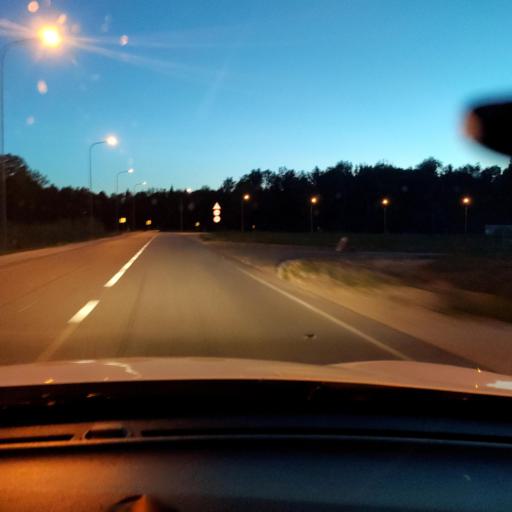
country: RU
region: Tatarstan
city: Osinovo
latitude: 55.8469
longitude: 48.8308
